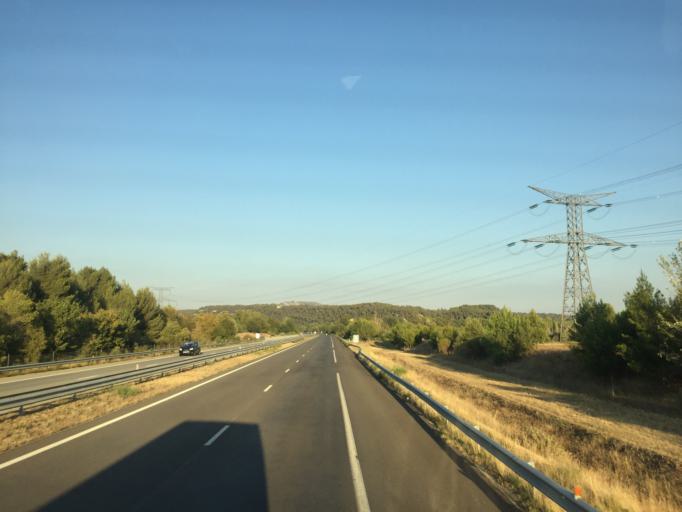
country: FR
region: Provence-Alpes-Cote d'Azur
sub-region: Departement des Bouches-du-Rhone
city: Peyrolles-en-Provence
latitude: 43.6572
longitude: 5.5939
